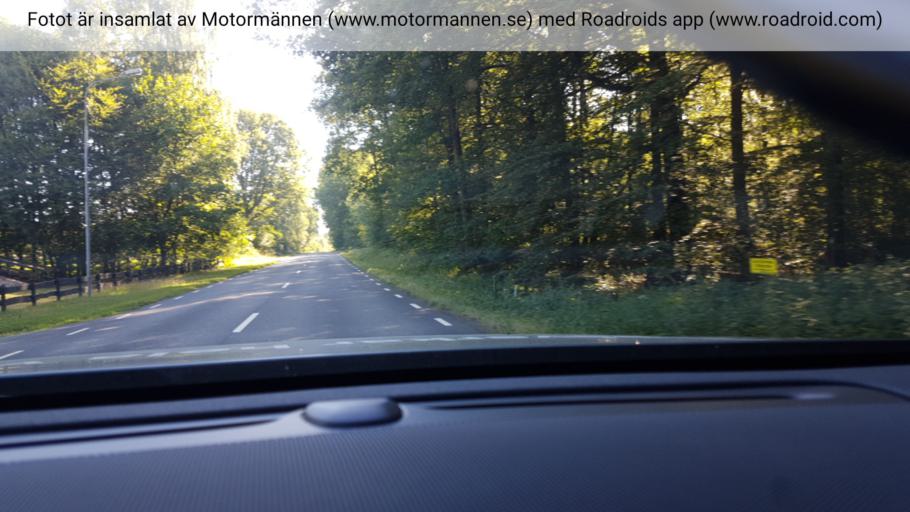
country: SE
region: Skane
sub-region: Hassleholms Kommun
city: Bjarnum
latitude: 56.3357
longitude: 13.6788
